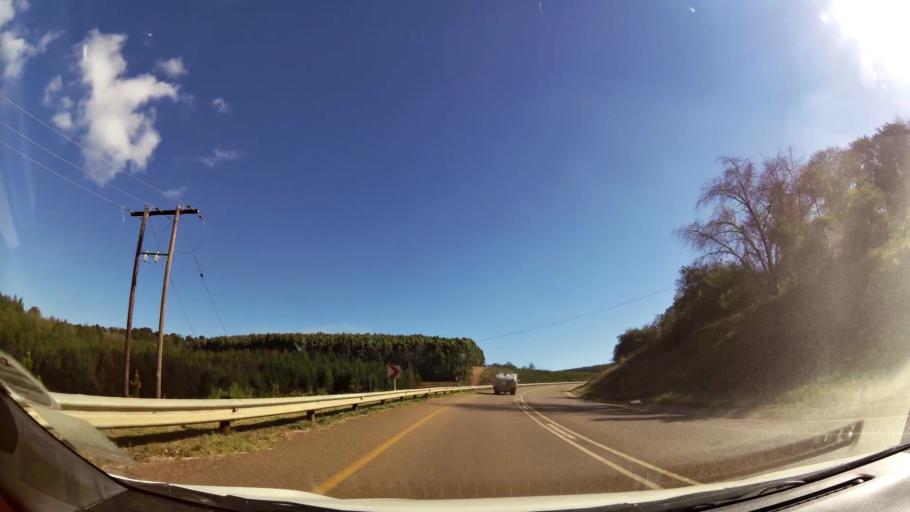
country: ZA
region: Limpopo
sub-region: Capricorn District Municipality
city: Mankoeng
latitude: -23.9111
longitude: 29.9734
